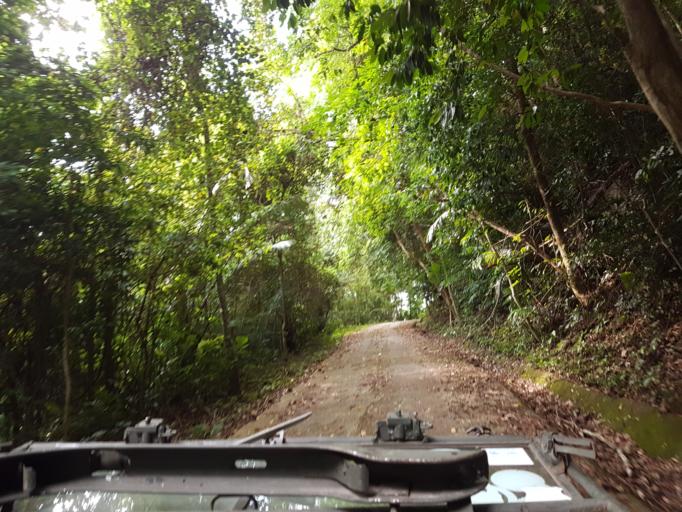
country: TH
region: Pattani
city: Khok Pho
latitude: 6.6571
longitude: 101.0983
